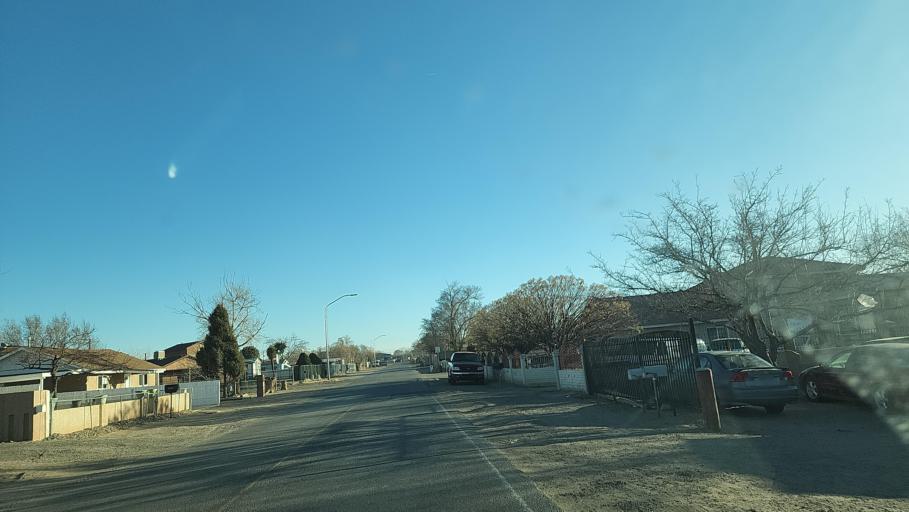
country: US
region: New Mexico
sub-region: Bernalillo County
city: South Valley
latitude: 35.0180
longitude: -106.6549
